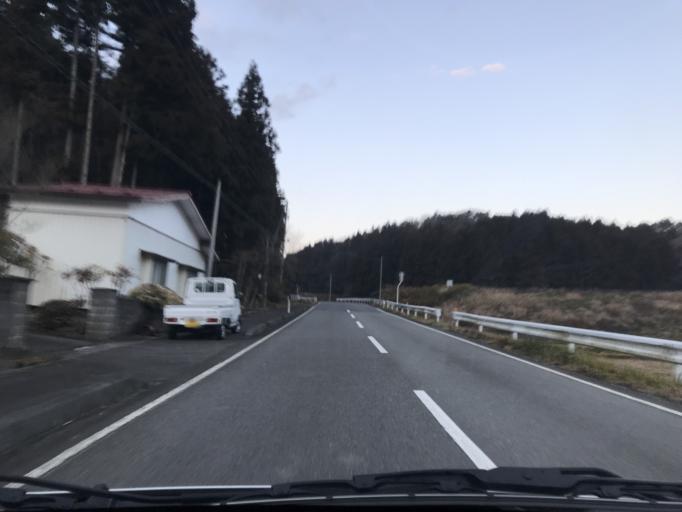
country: JP
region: Iwate
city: Ichinoseki
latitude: 38.8160
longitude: 141.1162
